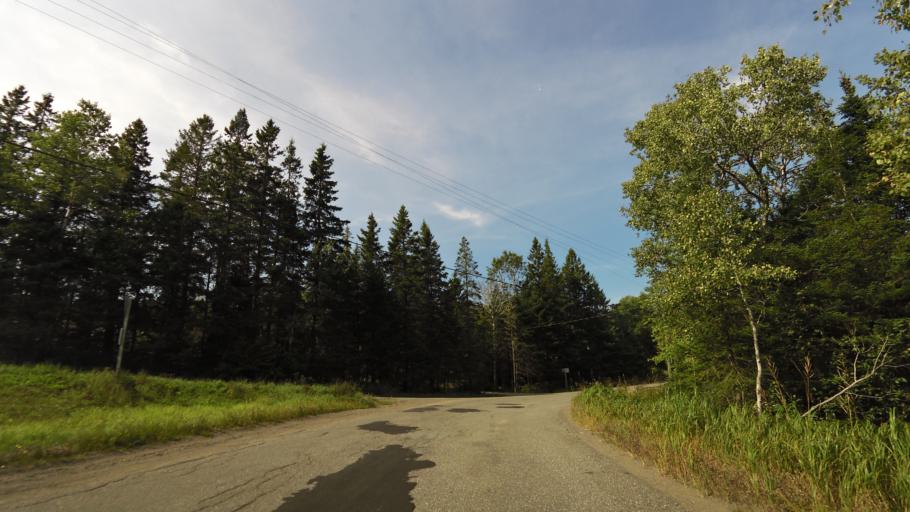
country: CA
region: New Brunswick
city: Hampton
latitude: 45.5695
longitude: -65.9076
